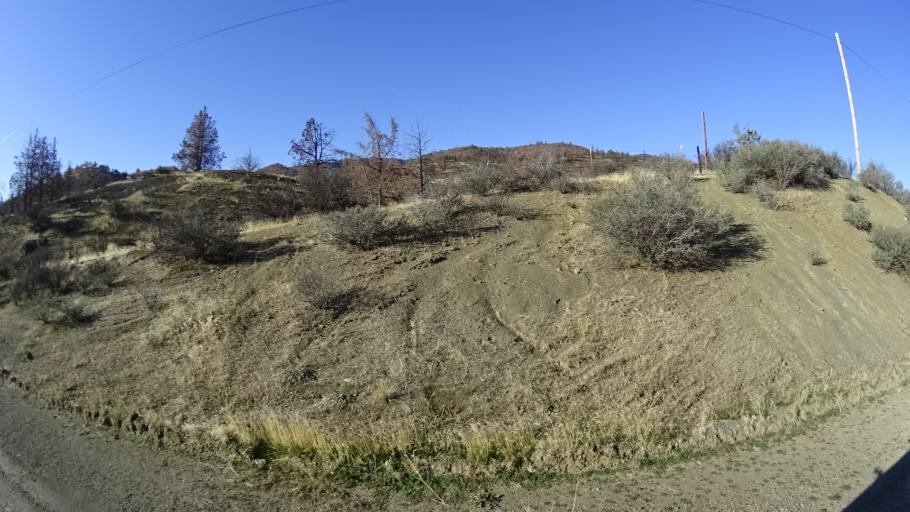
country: US
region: California
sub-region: Siskiyou County
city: Montague
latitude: 41.8990
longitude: -122.5674
